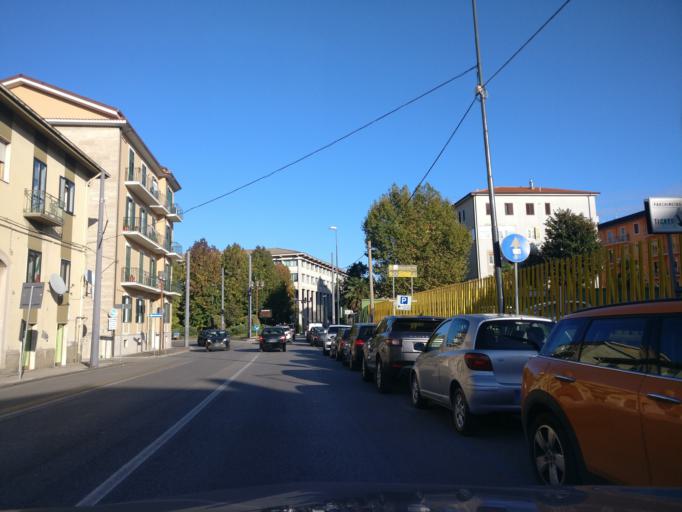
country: IT
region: Campania
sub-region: Provincia di Avellino
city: Avellino
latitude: 40.9152
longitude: 14.7842
